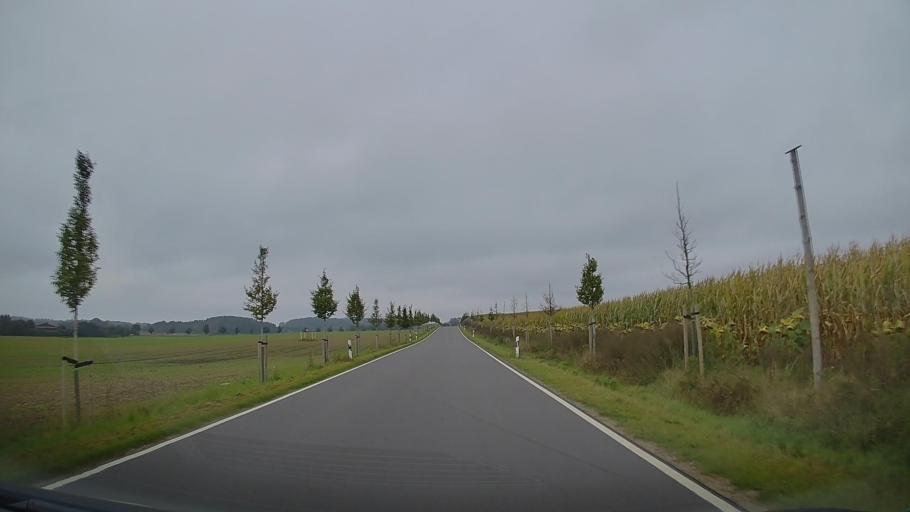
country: DE
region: Mecklenburg-Vorpommern
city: Dummerstorf
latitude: 53.9589
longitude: 12.2358
